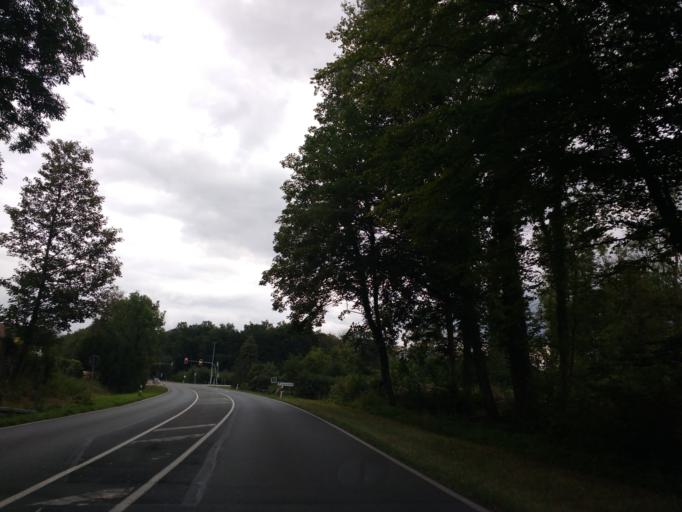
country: DE
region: Lower Saxony
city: Bad Rothenfelde
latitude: 52.1019
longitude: 8.1561
